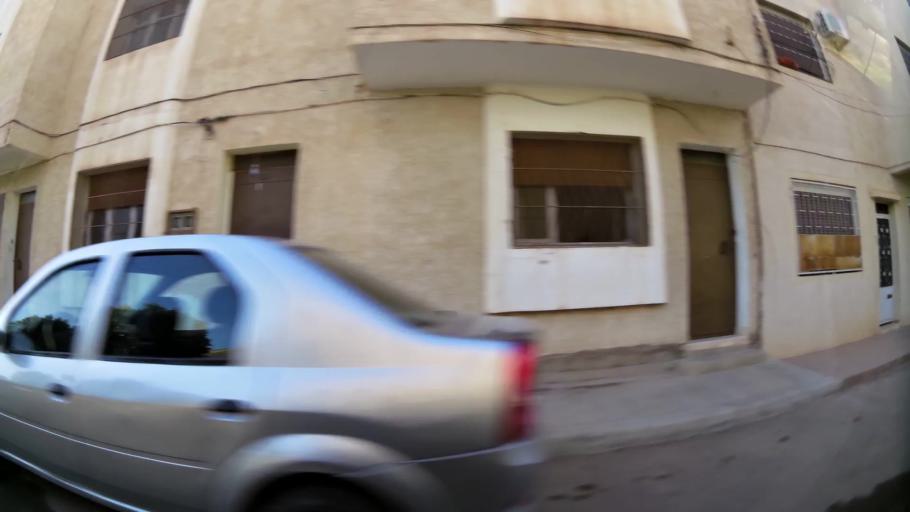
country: MA
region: Oriental
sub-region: Oujda-Angad
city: Oujda
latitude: 34.6783
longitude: -1.8935
